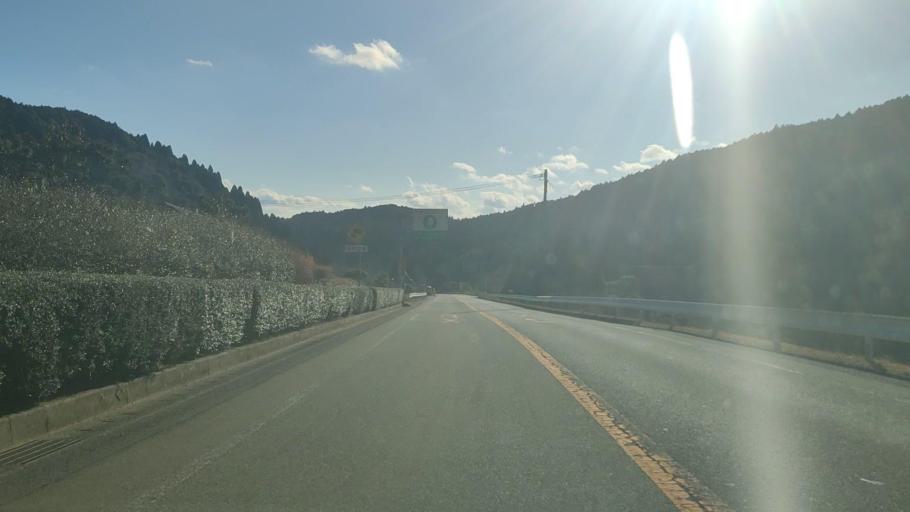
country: JP
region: Fukuoka
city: Maebaru-chuo
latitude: 33.4623
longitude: 130.2750
